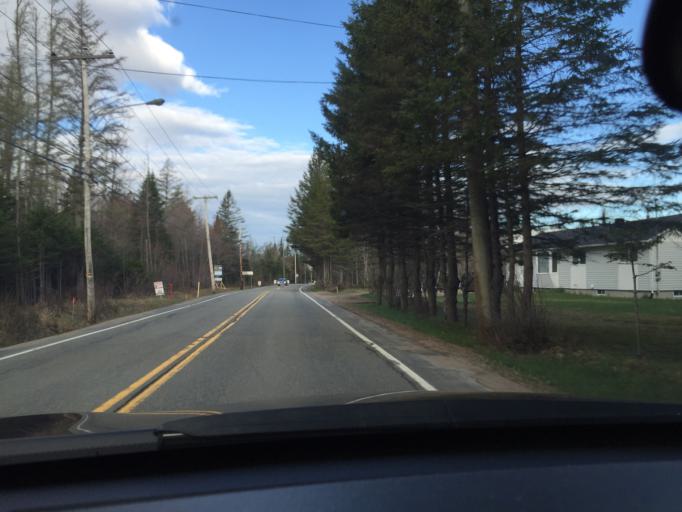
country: CA
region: Quebec
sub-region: Capitale-Nationale
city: Sainte Catherine de la Jacques Cartier
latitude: 46.8476
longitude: -71.5931
